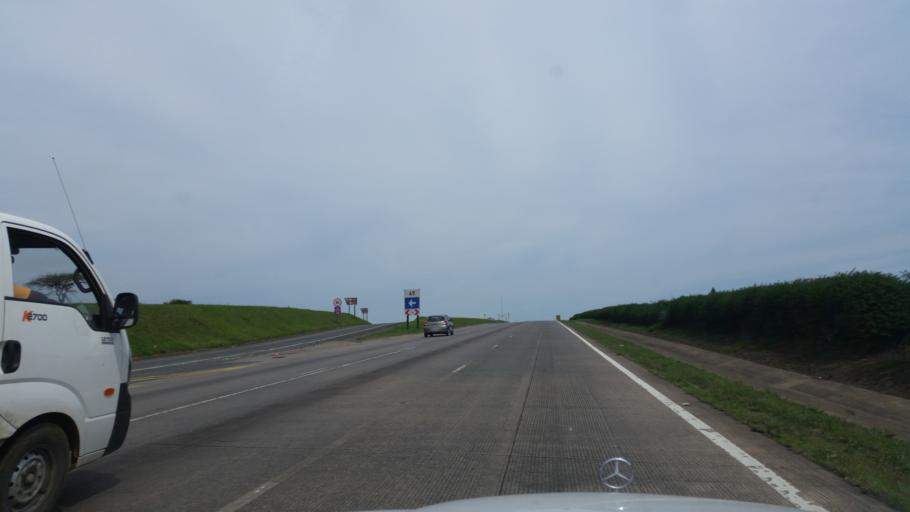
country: ZA
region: KwaZulu-Natal
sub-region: uMgungundlovu District Municipality
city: Camperdown
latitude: -29.6885
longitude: 30.4796
